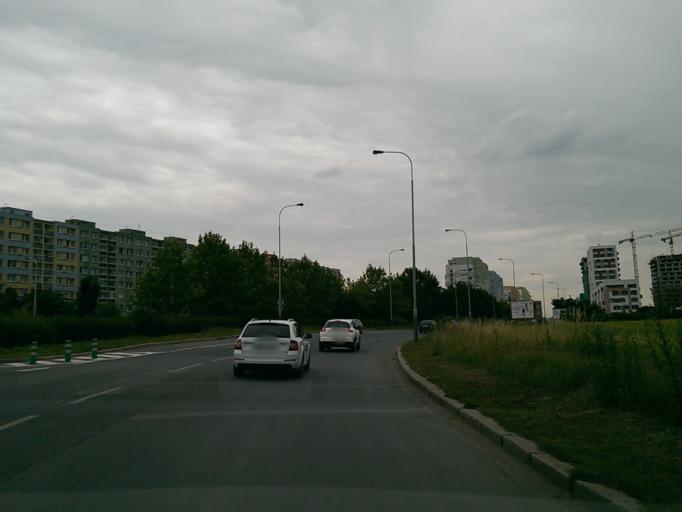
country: CZ
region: Central Bohemia
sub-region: Okres Praha-Zapad
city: Pruhonice
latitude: 50.0369
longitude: 14.5668
